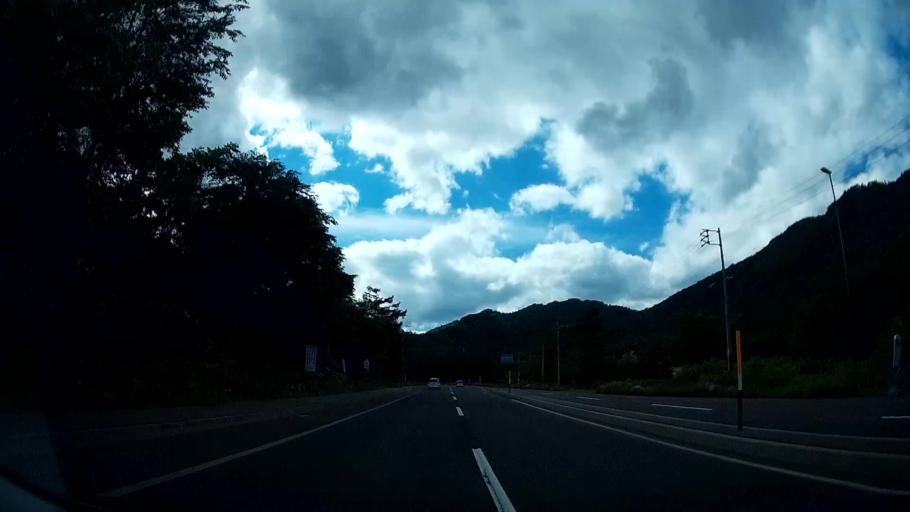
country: JP
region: Hokkaido
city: Sapporo
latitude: 42.9688
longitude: 141.1931
